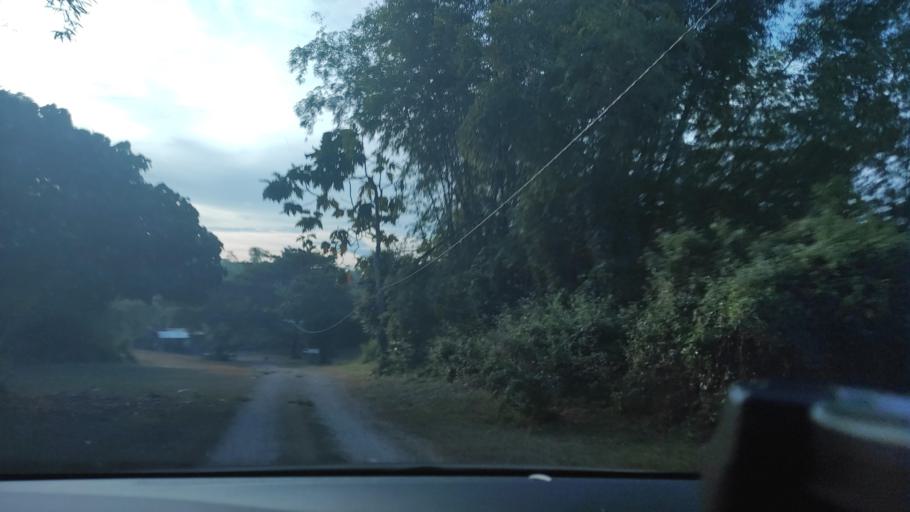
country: PH
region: Ilocos
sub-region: Province of Pangasinan
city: Balingasay
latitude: 16.3088
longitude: 119.8684
